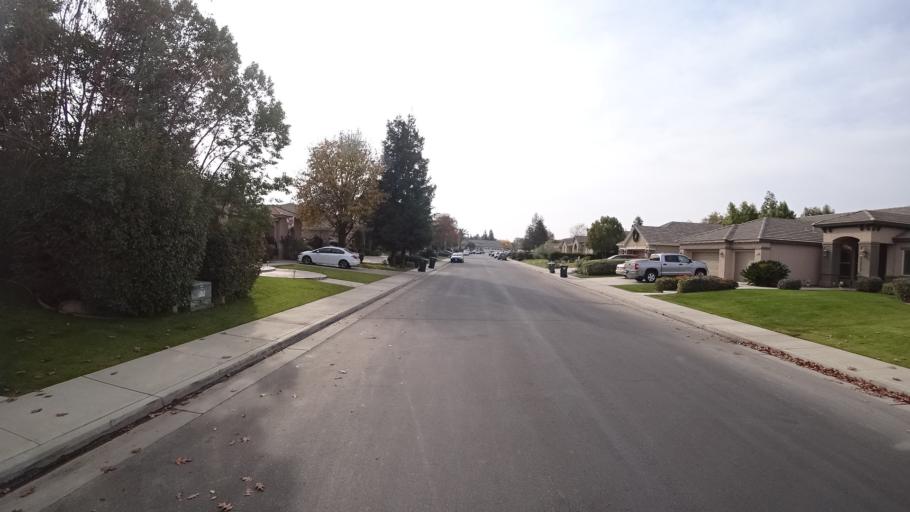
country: US
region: California
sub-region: Kern County
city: Rosedale
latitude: 35.3454
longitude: -119.1380
